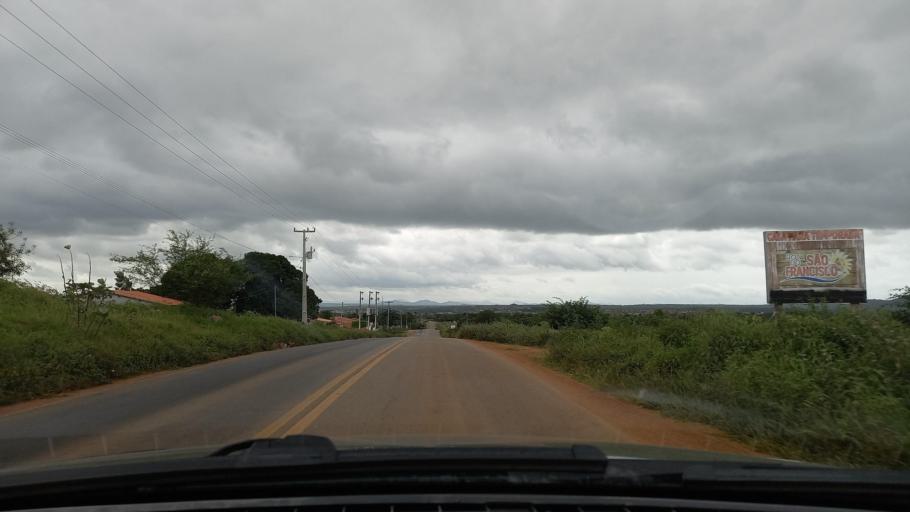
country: BR
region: Sergipe
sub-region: Caninde De Sao Francisco
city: Caninde de Sao Francisco
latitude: -9.6833
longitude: -37.8120
